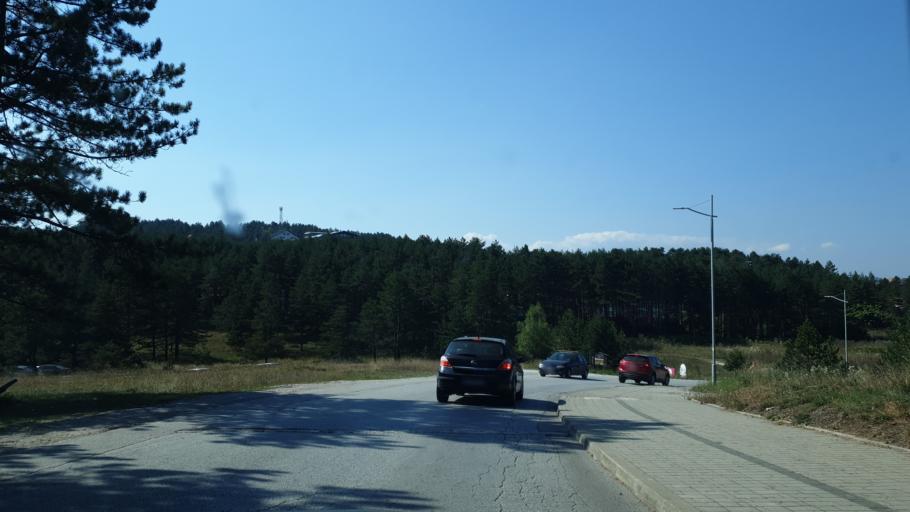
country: RS
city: Zlatibor
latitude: 43.7214
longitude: 19.7073
